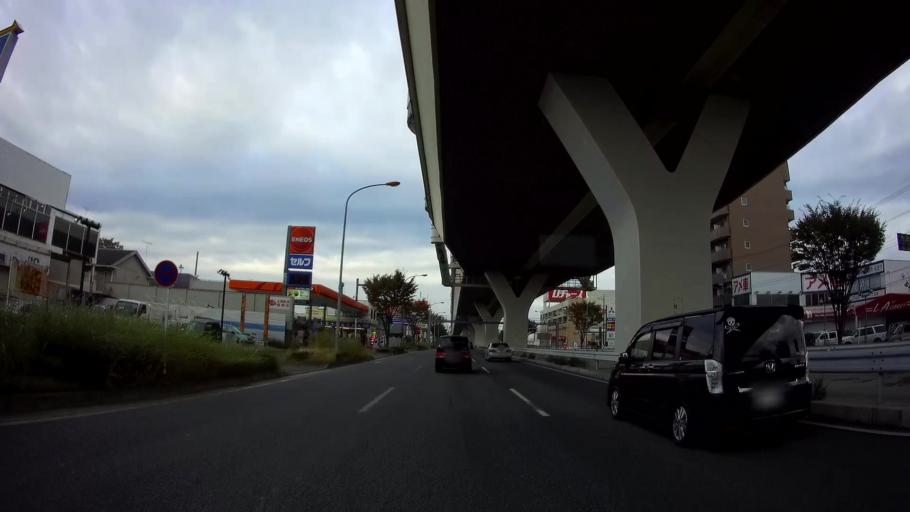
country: JP
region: Saitama
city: Wako
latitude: 35.8288
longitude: 139.6365
